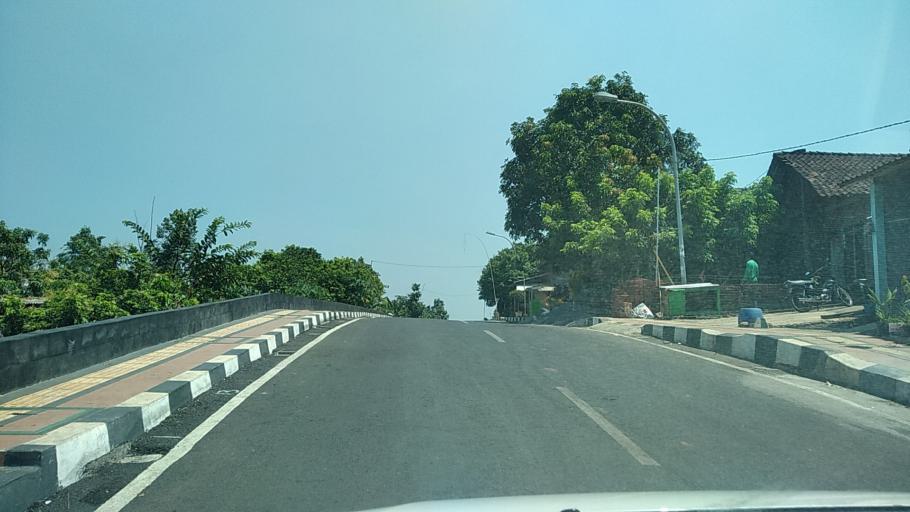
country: ID
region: Central Java
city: Ungaran
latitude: -7.0870
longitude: 110.3599
